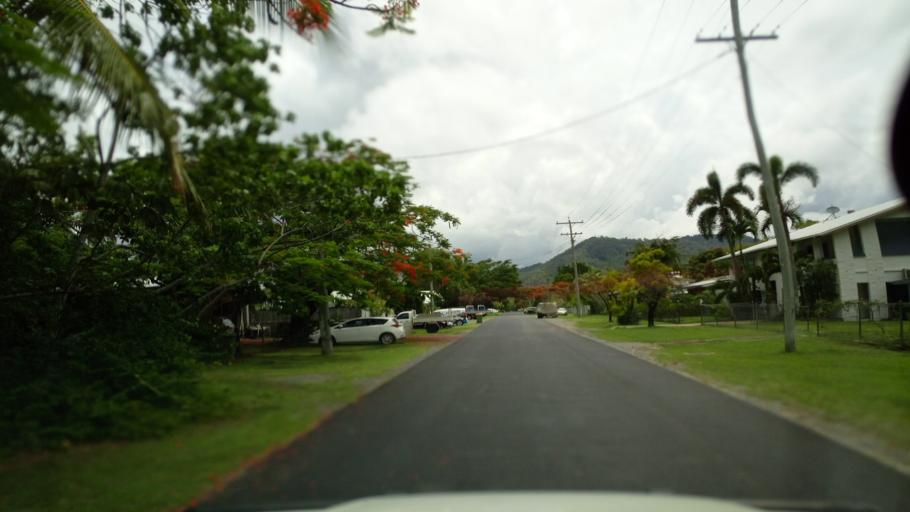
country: AU
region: Queensland
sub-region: Cairns
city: Redlynch
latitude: -16.8555
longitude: 145.7454
